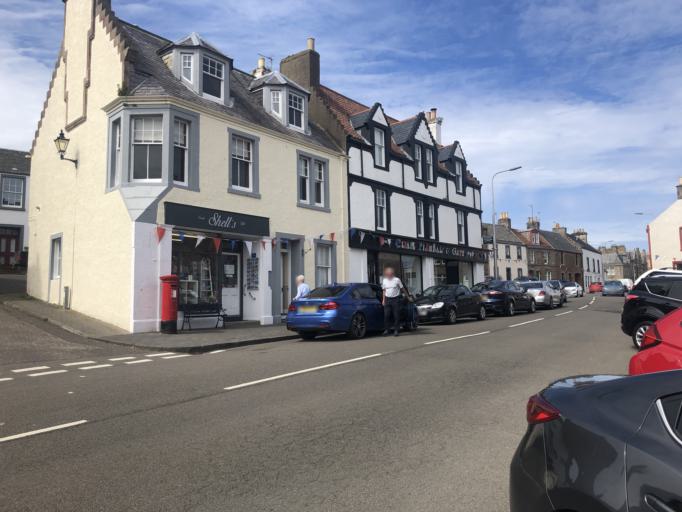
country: GB
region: Scotland
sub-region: Fife
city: Anstruther
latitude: 56.2594
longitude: -2.6278
